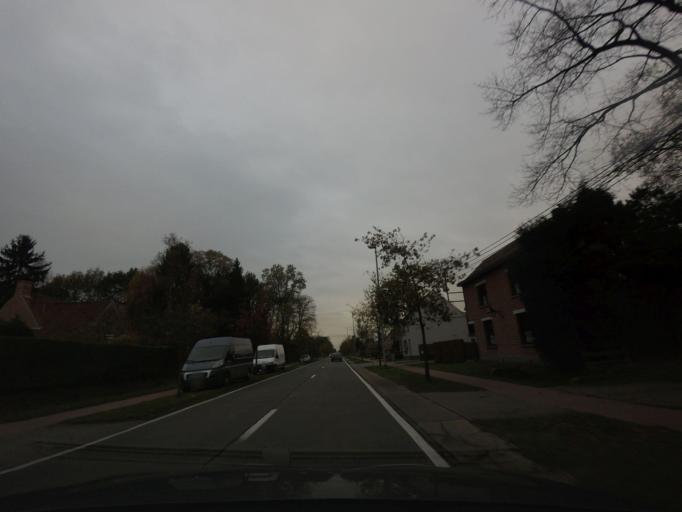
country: BE
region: Flanders
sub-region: Provincie Antwerpen
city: Brecht
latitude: 51.3197
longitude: 4.5907
